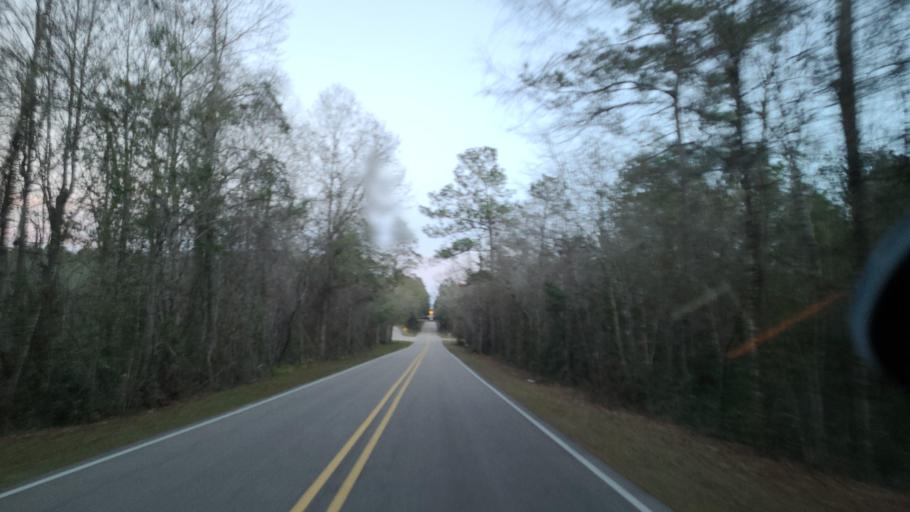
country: US
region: Mississippi
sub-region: Forrest County
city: Hattiesburg
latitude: 31.2115
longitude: -89.2557
